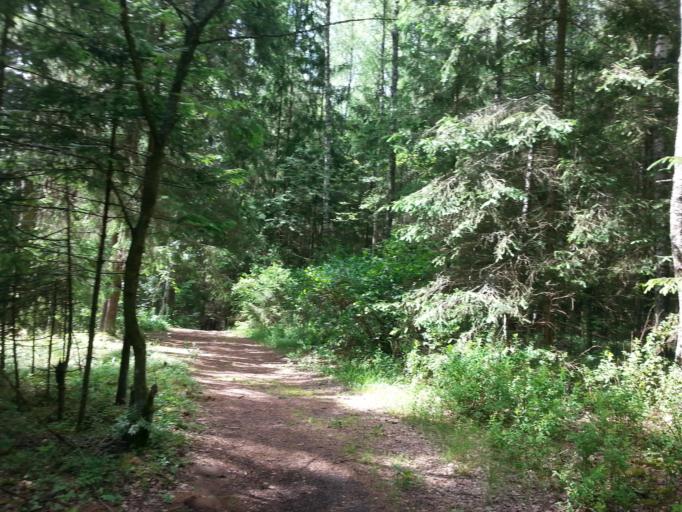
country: BY
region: Minsk
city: Svir
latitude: 54.9644
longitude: 26.3845
